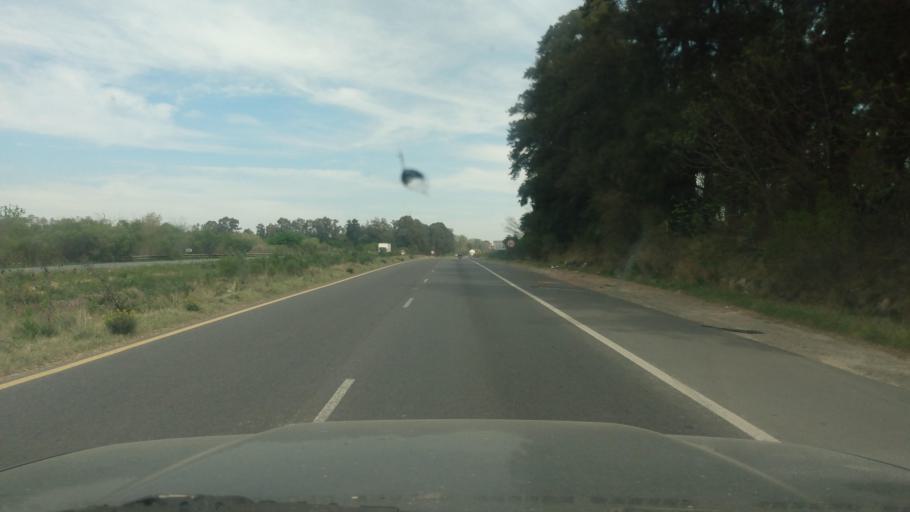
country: AR
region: Buenos Aires
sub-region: Partido de Lujan
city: Lujan
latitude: -34.4521
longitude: -59.0551
